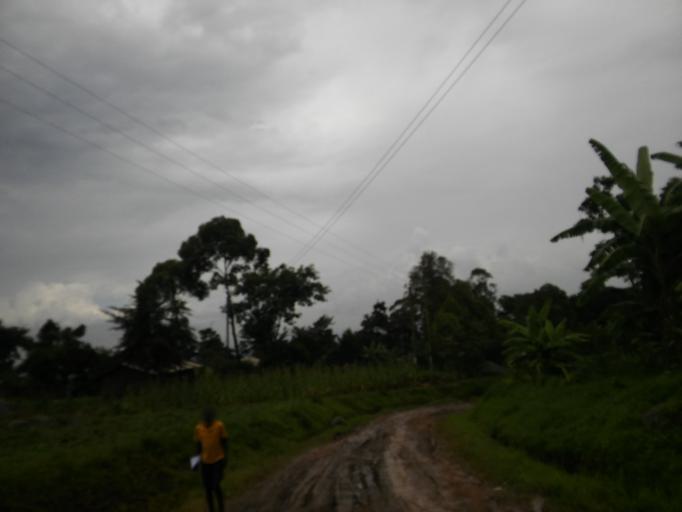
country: UG
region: Eastern Region
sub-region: Bududa District
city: Bududa
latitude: 1.0042
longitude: 34.2444
